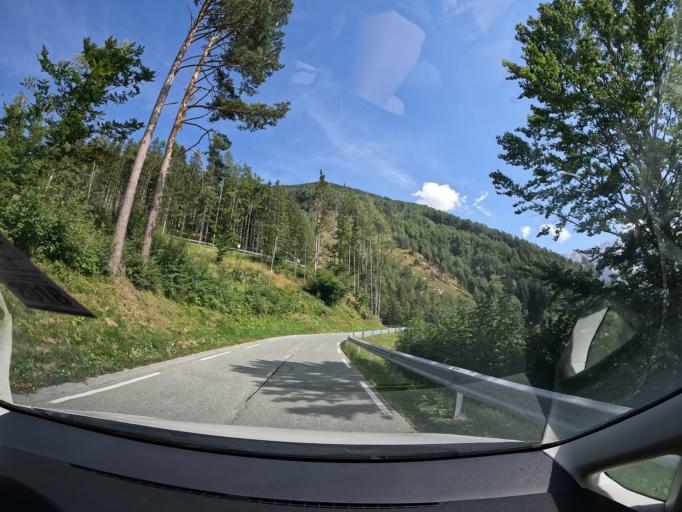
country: AT
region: Carinthia
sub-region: Politischer Bezirk Sankt Veit an der Glan
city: Liebenfels
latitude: 46.7069
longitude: 14.2817
